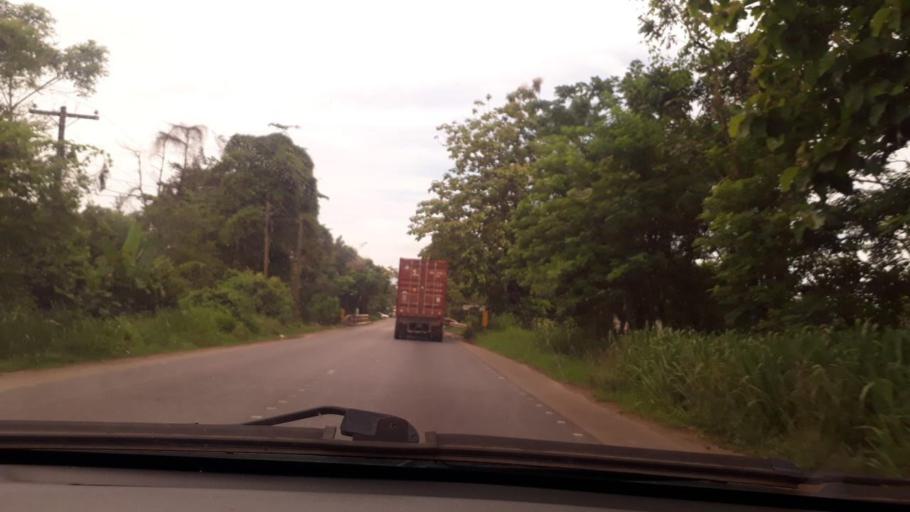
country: GT
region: Izabal
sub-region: Municipio de Puerto Barrios
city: Puerto Barrios
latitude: 15.5883
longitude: -88.5781
